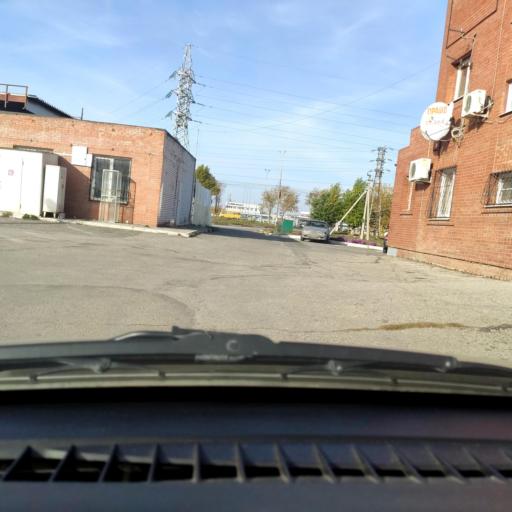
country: RU
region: Samara
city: Tol'yatti
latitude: 53.5457
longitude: 49.2875
